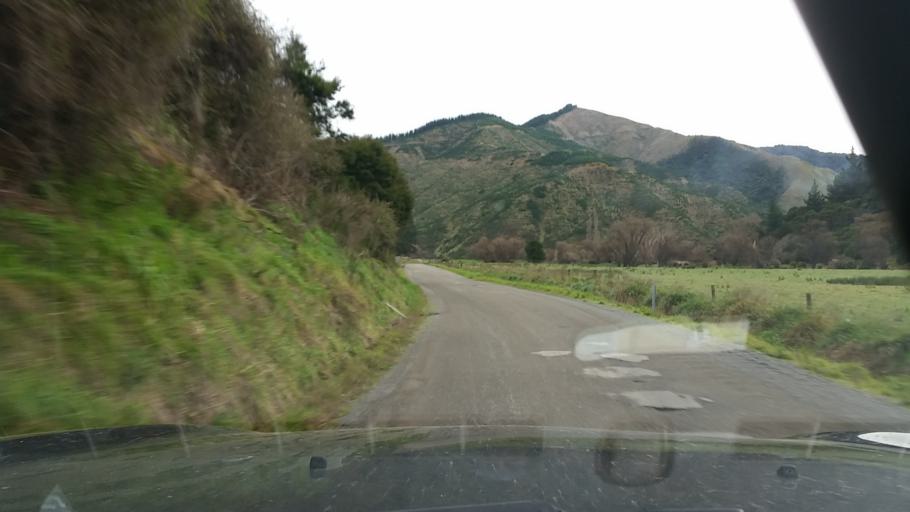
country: NZ
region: Marlborough
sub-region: Marlborough District
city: Blenheim
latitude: -41.4225
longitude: 173.8903
